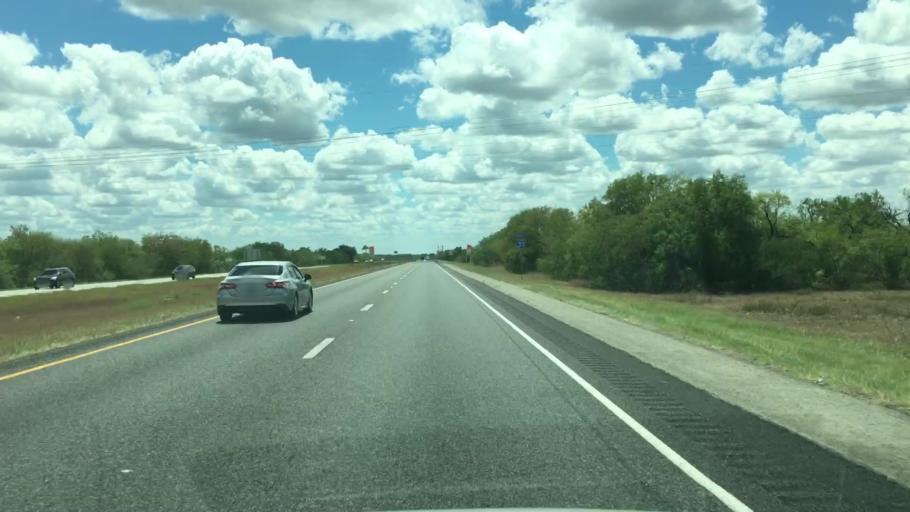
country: US
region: Texas
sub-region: Atascosa County
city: Pleasanton
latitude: 28.9858
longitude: -98.4323
